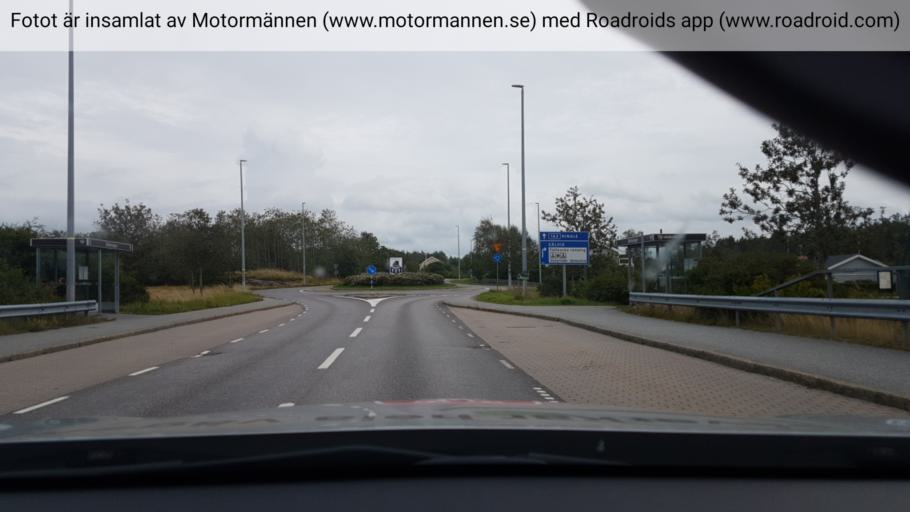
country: SE
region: Vaestra Goetaland
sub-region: Tanums Kommun
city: Grebbestad
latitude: 58.5992
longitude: 11.2914
